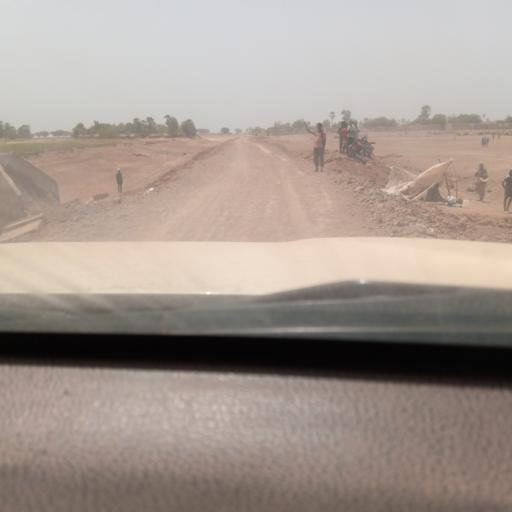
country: ML
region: Mopti
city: Tenenkou
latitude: 14.4315
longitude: -4.8786
